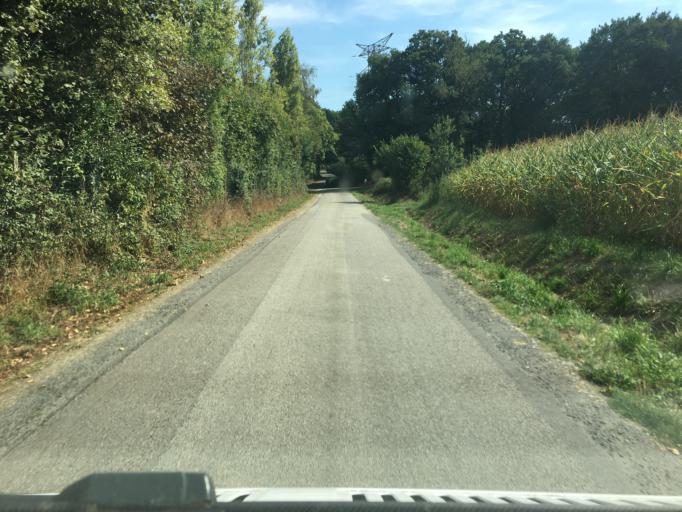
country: FR
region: Brittany
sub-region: Departement des Cotes-d'Armor
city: Mur-de-Bretagne
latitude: 48.2060
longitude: -3.0044
